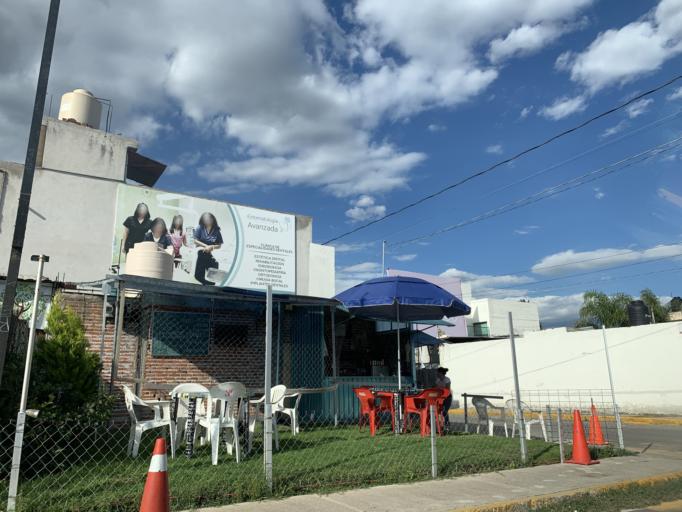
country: MX
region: Puebla
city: San Andres Cholula
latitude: 19.0542
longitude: -98.3092
